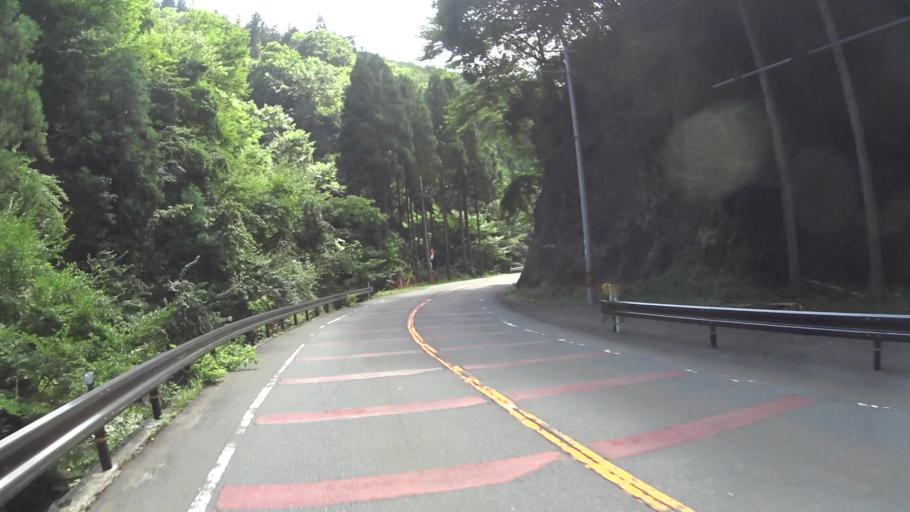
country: JP
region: Fukui
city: Obama
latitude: 35.3495
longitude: 135.5952
